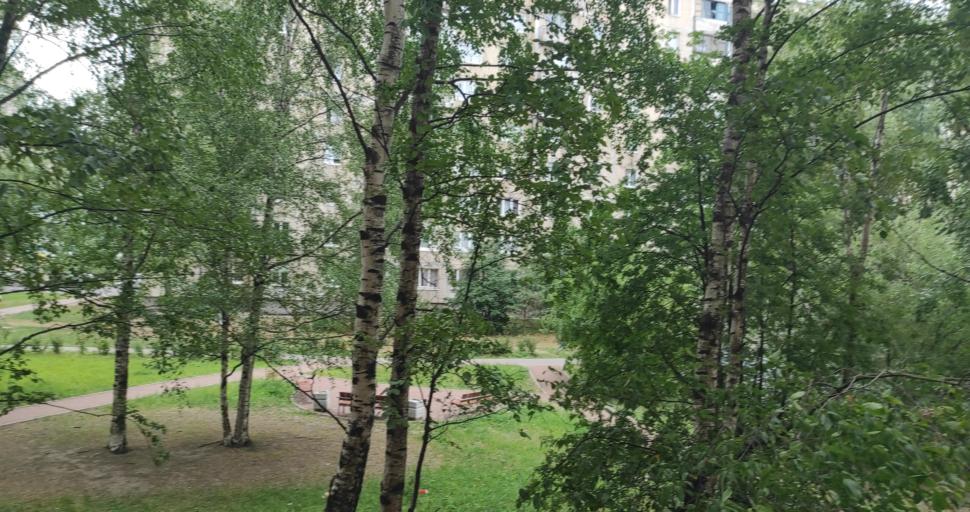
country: RU
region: St.-Petersburg
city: Krasnogvargeisky
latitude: 59.9138
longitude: 30.4568
